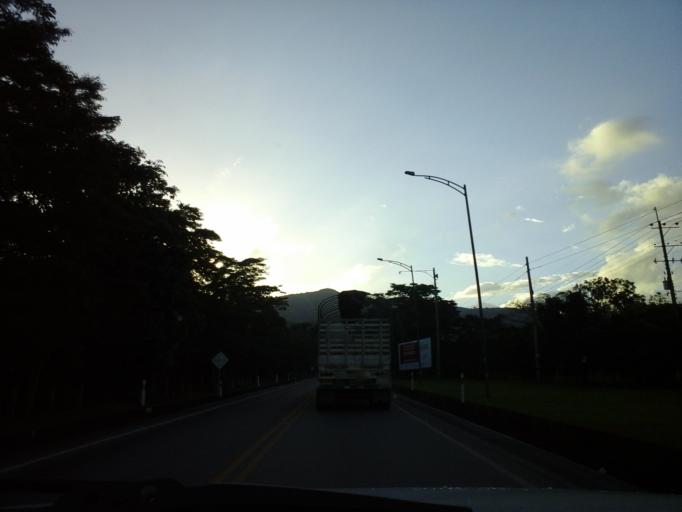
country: CO
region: Meta
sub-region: Villavicencio
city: Villavicencio
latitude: 4.1239
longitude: -73.6480
